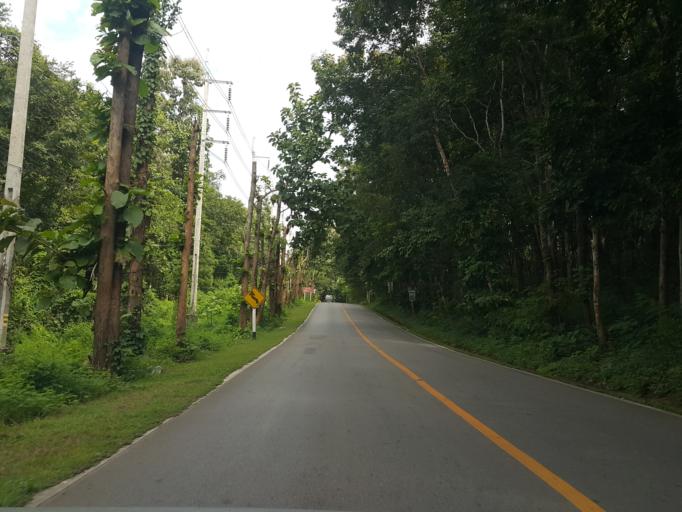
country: TH
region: Mae Hong Son
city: Mae Hong Son
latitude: 19.3745
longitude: 97.9625
